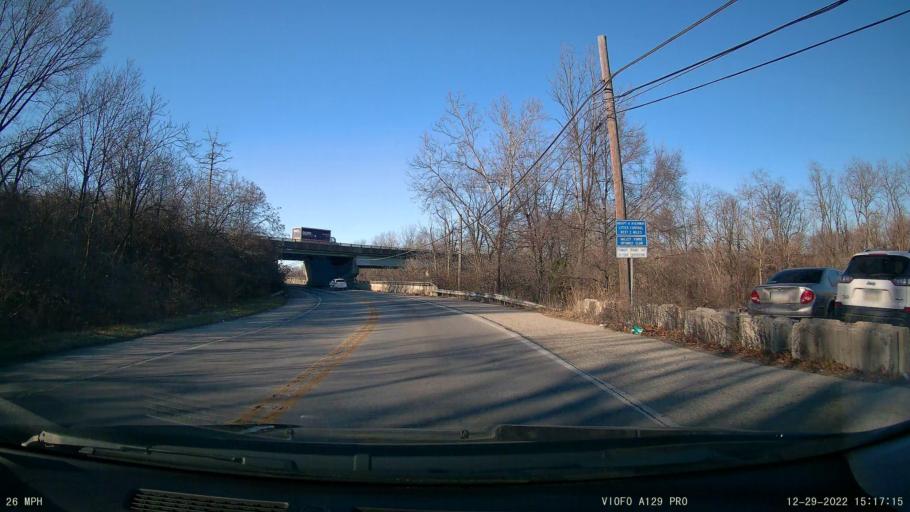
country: US
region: Pennsylvania
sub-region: Montgomery County
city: Bridgeport
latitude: 40.1069
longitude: -75.3503
